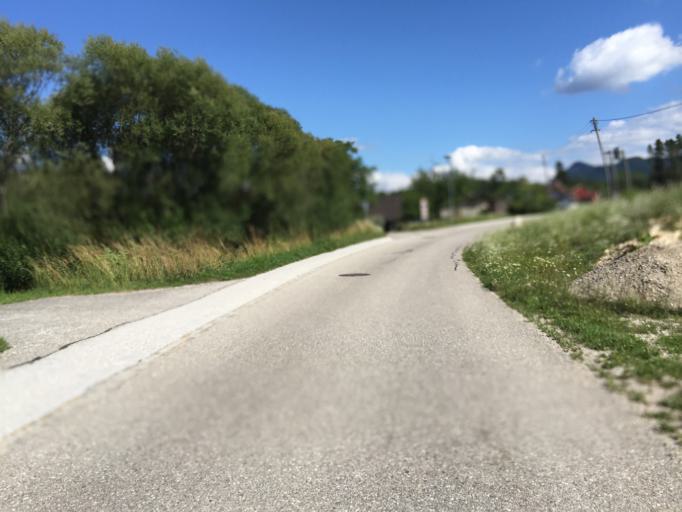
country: AT
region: Carinthia
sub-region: Politischer Bezirk Volkermarkt
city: Feistritz ob Bleiburg
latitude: 46.5598
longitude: 14.7637
